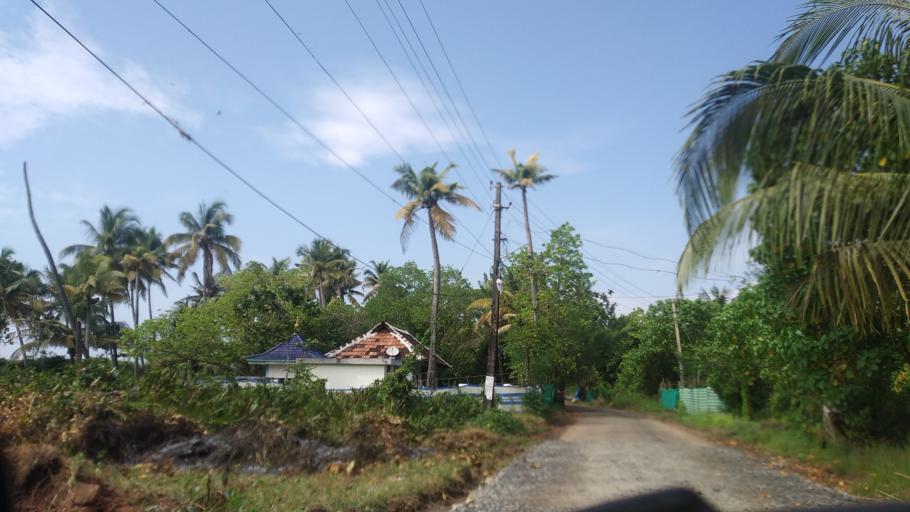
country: IN
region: Kerala
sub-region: Ernakulam
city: Elur
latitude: 10.0678
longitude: 76.1984
